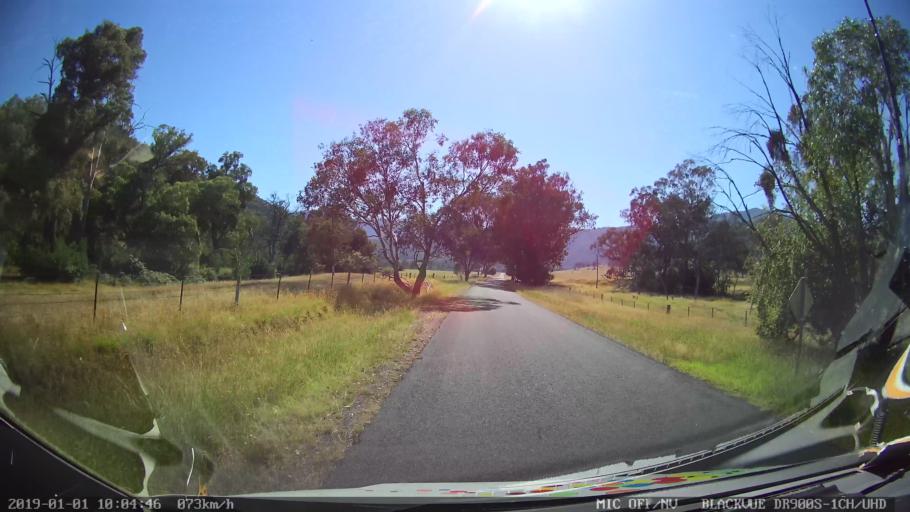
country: AU
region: New South Wales
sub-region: Snowy River
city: Jindabyne
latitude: -36.1750
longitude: 148.1267
